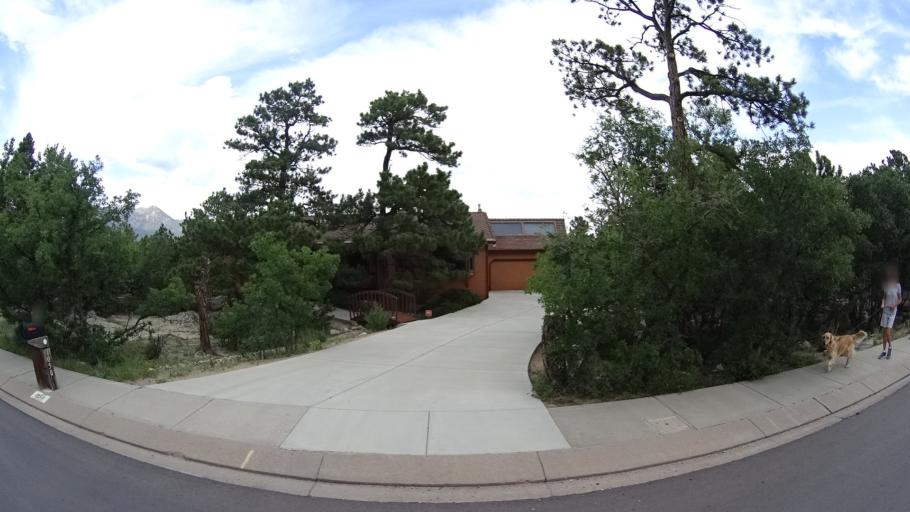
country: US
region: Colorado
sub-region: El Paso County
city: Colorado Springs
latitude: 38.9060
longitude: -104.8465
